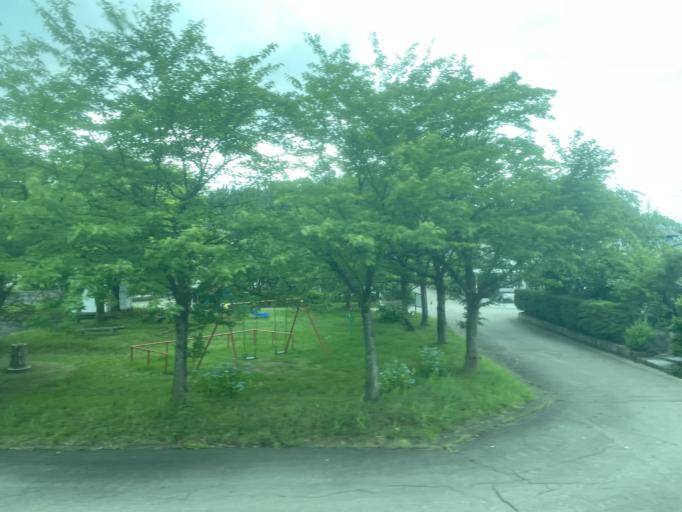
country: JP
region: Niigata
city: Nagaoka
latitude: 37.5270
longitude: 138.7133
